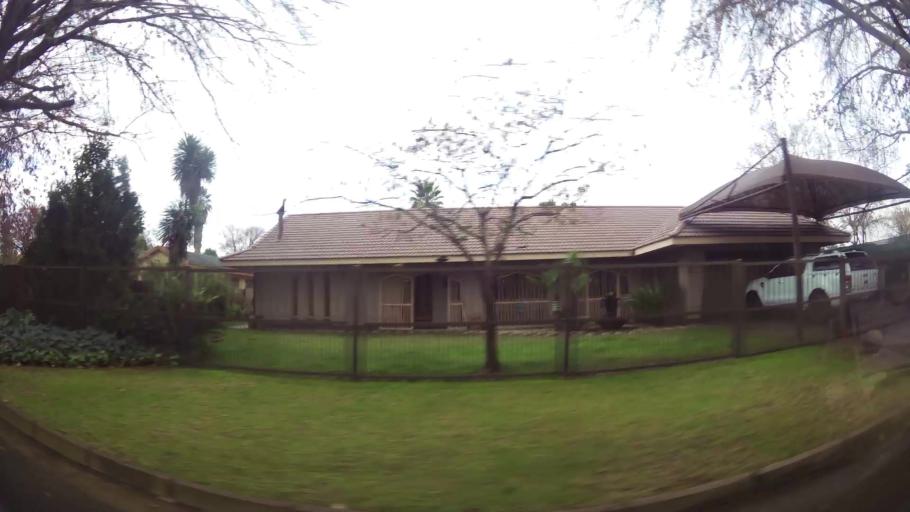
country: ZA
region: Gauteng
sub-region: Sedibeng District Municipality
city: Vereeniging
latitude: -26.6427
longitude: 27.9745
